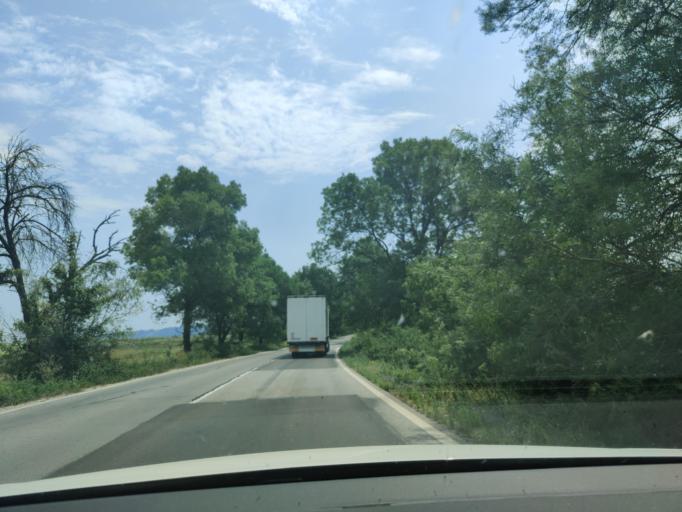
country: BG
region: Vidin
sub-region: Obshtina Ruzhintsi
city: Ruzhintsi
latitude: 43.6342
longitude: 22.8183
